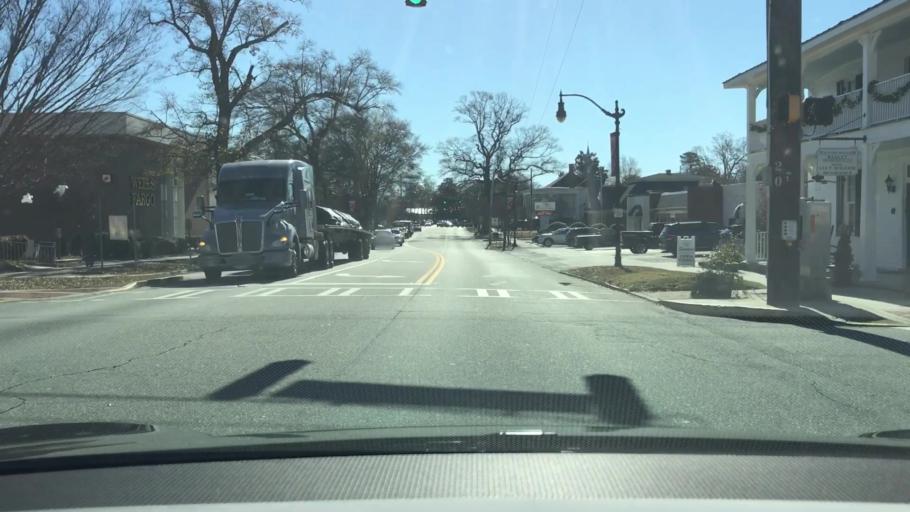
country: US
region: Georgia
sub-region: Walton County
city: Monroe
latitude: 33.7935
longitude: -83.7130
